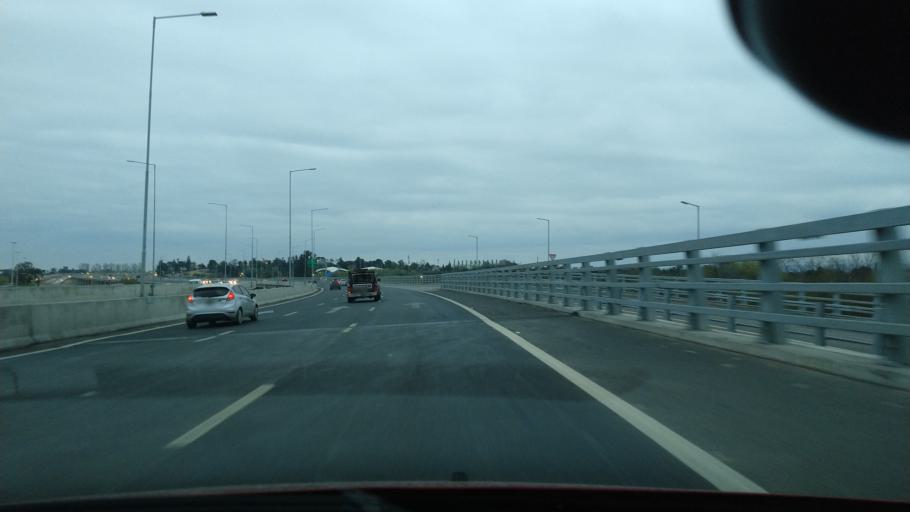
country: AR
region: Cordoba
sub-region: Departamento de Capital
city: Cordoba
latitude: -31.3647
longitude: -64.2481
